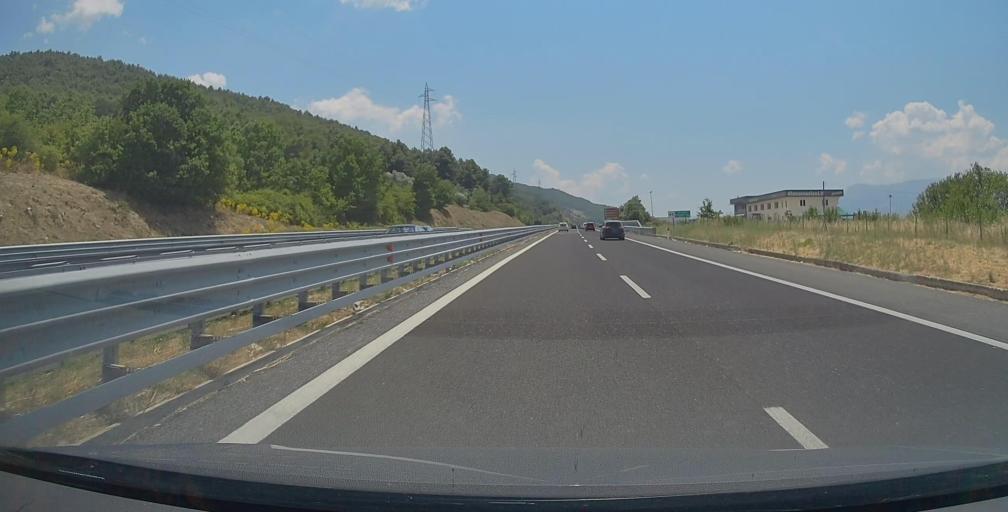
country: IT
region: Campania
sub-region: Provincia di Salerno
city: Atena Lucana
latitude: 40.4848
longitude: 15.5326
